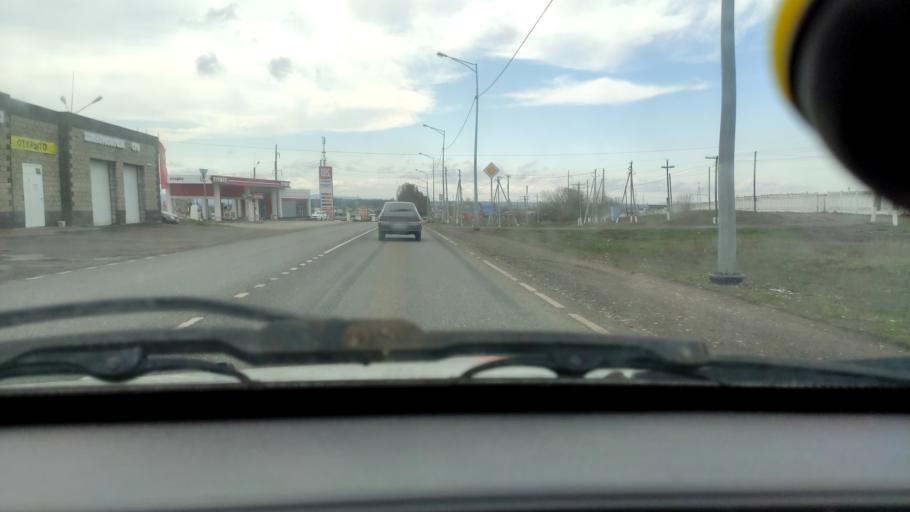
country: RU
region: Samara
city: Zhigulevsk
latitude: 53.5573
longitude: 49.5360
